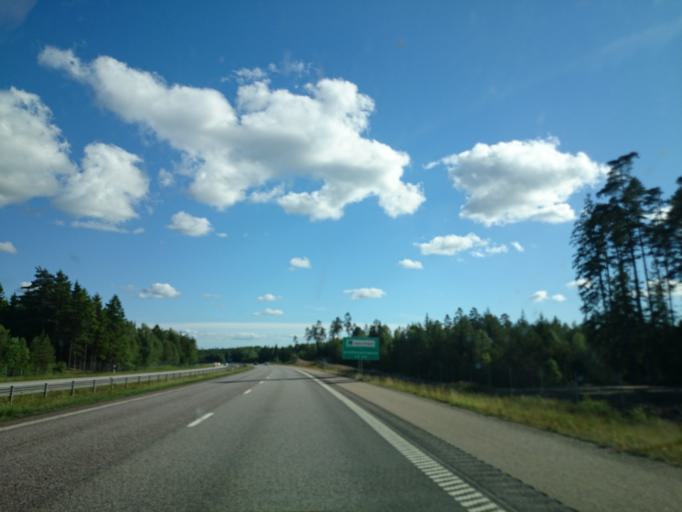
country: SE
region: Kronoberg
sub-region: Markaryds Kommun
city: Stromsnasbruk
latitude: 56.5813
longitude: 13.7212
